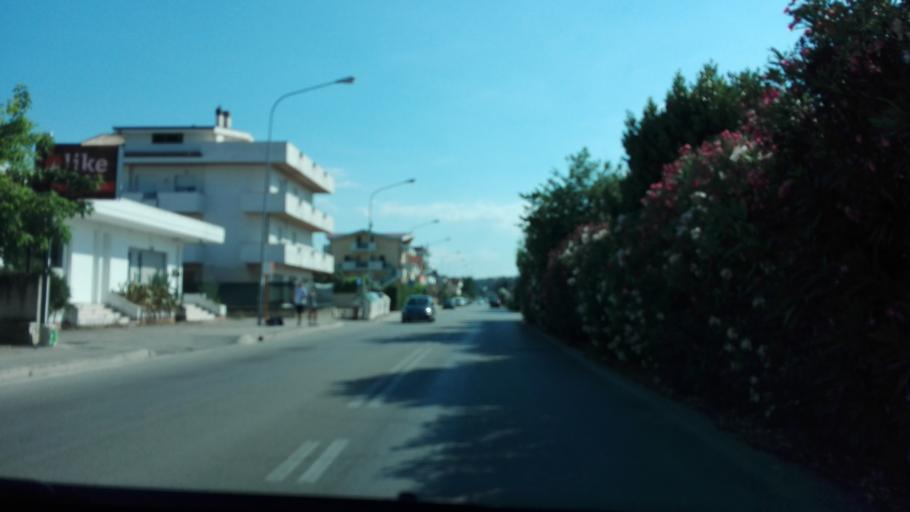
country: IT
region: Abruzzo
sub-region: Provincia di Pescara
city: Cappelle sul Tavo
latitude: 42.4854
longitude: 14.1185
